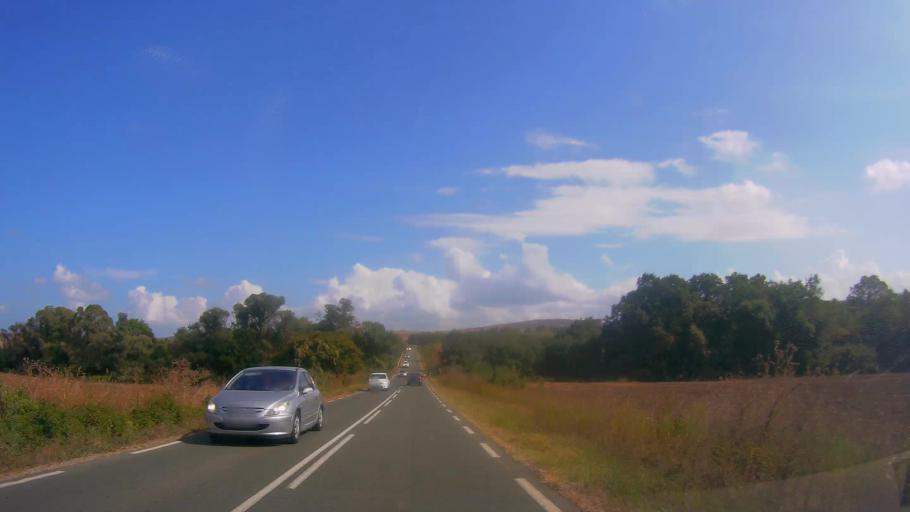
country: BG
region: Burgas
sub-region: Obshtina Burgas
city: Burgas
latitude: 42.4763
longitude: 27.3565
